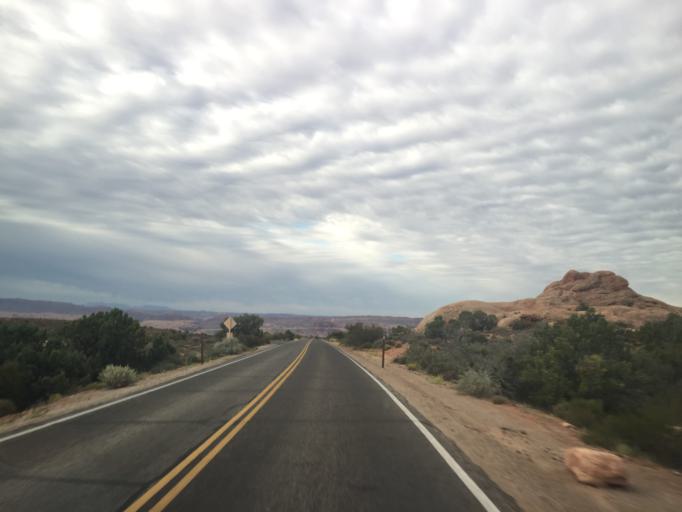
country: US
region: Utah
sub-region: Grand County
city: Moab
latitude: 38.6988
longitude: -109.5712
